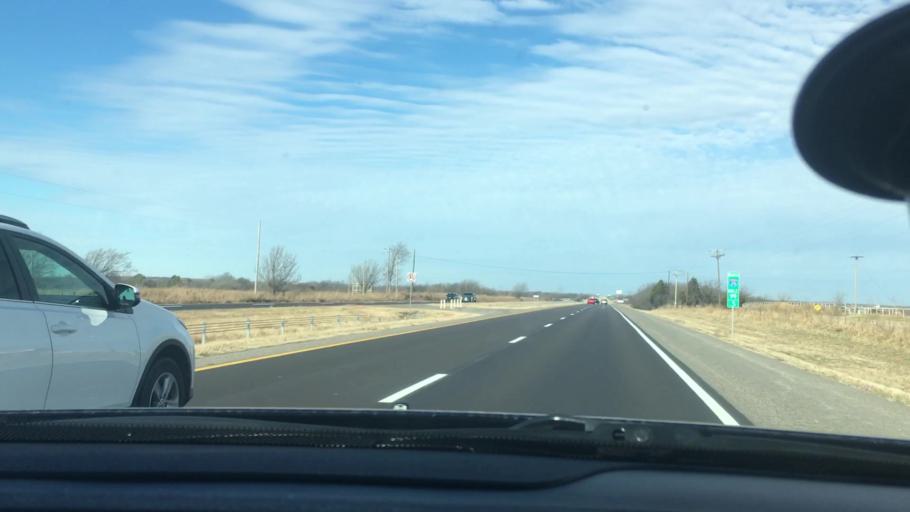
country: US
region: Oklahoma
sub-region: Cleveland County
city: Noble
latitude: 35.0945
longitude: -97.4224
